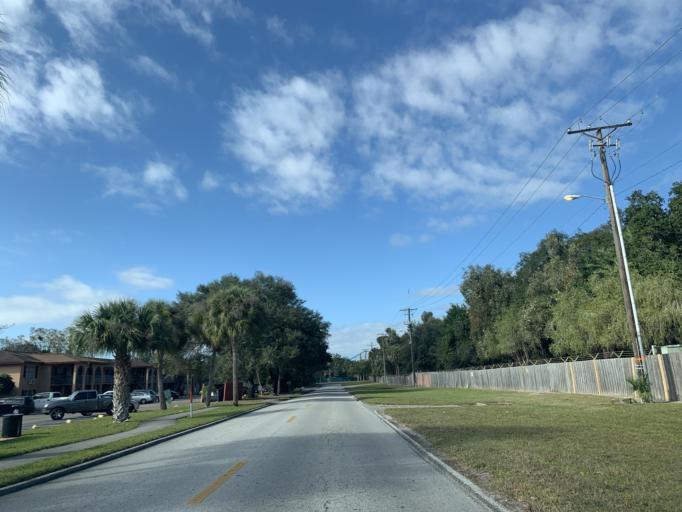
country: US
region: Florida
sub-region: Hillsborough County
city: Temple Terrace
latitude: 28.0399
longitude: -82.4135
